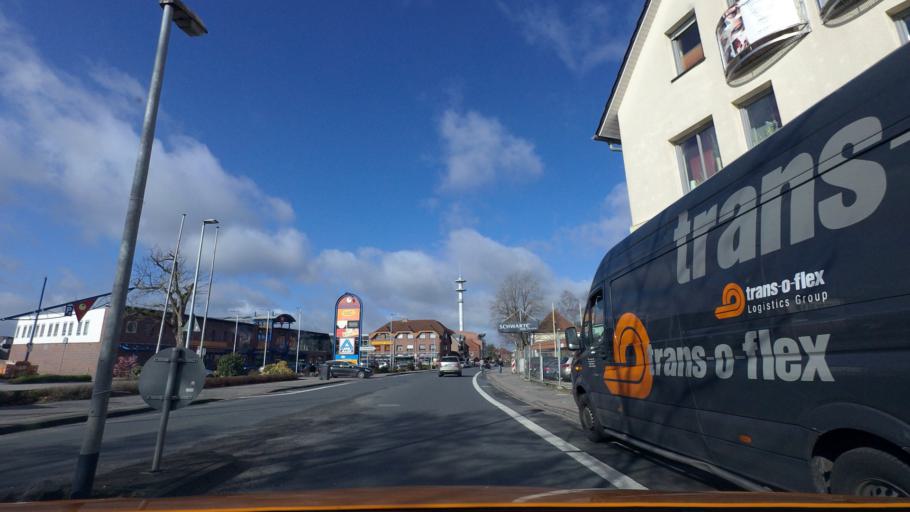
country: DE
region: Lower Saxony
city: Cloppenburg
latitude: 52.8433
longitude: 8.0523
